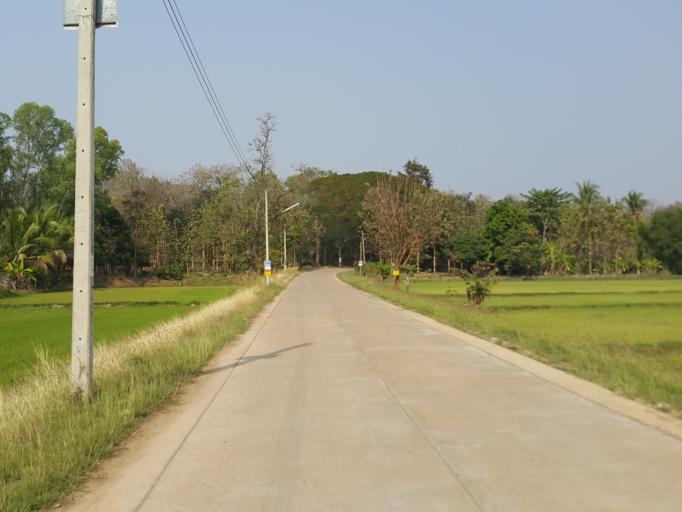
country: TH
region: Sukhothai
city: Thung Saliam
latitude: 17.3297
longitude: 99.5348
